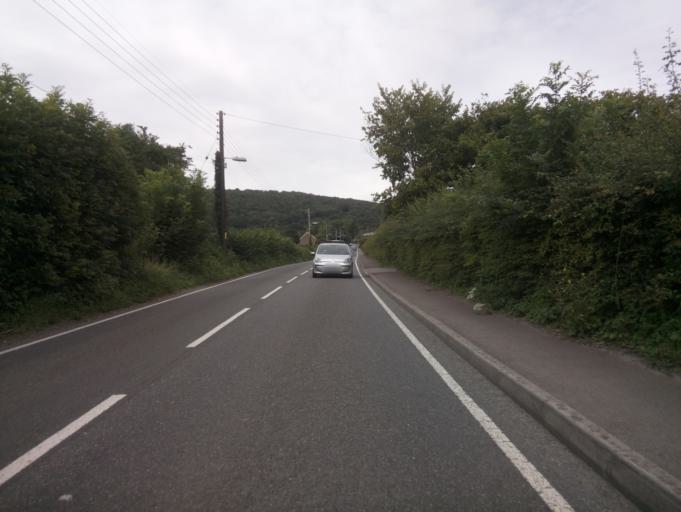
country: GB
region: England
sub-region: Somerset
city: Cheddar
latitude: 51.2848
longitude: -2.7900
